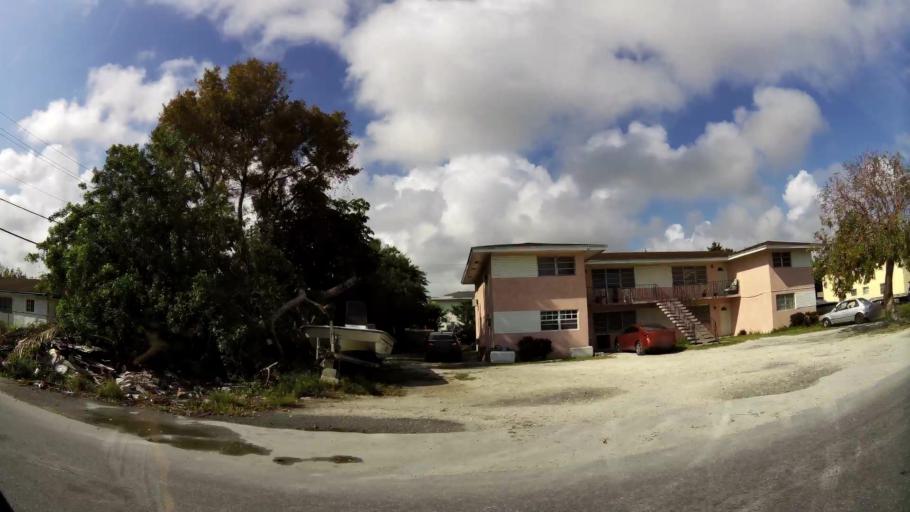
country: BS
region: Freeport
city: Lucaya
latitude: 26.5217
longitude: -78.6782
